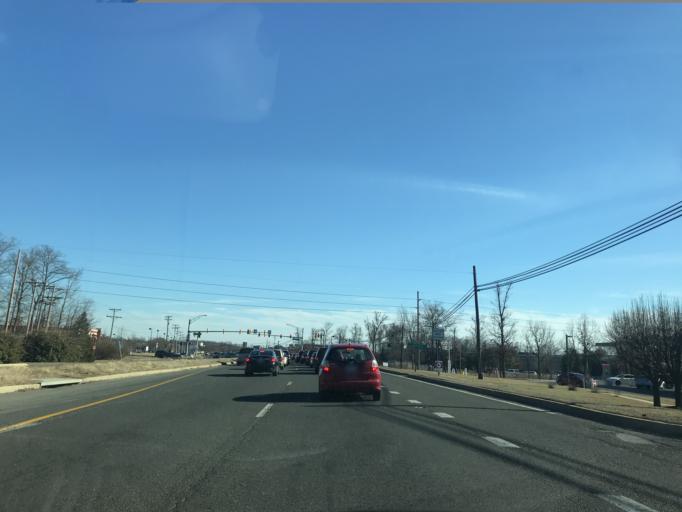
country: US
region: Maryland
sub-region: Charles County
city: Waldorf
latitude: 38.6306
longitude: -76.9189
